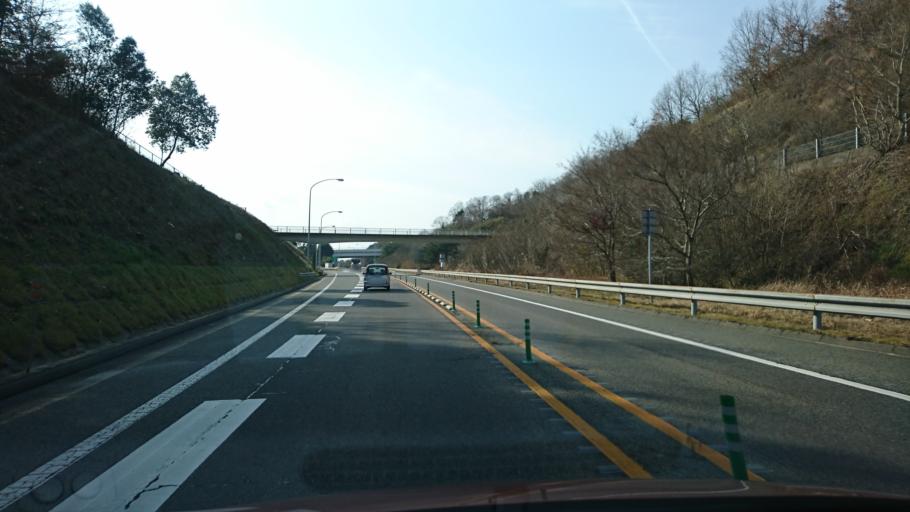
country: JP
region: Hiroshima
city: Onomichi
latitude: 34.3835
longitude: 133.1954
